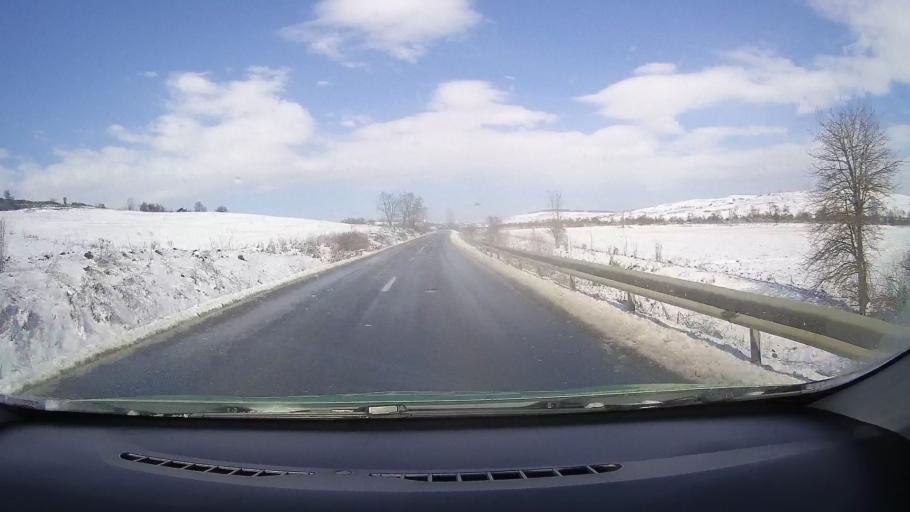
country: RO
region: Sibiu
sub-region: Comuna Nocrich
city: Nocrich
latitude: 45.9041
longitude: 24.4644
